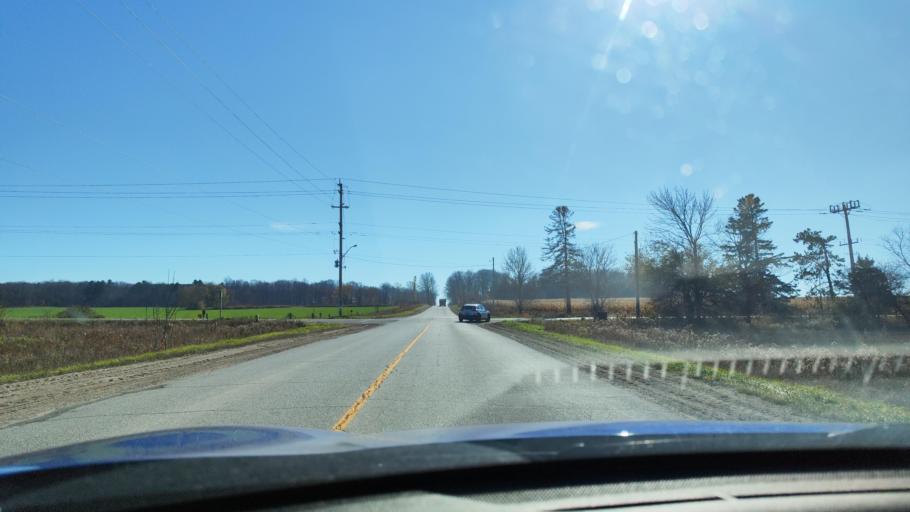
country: CA
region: Ontario
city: Wasaga Beach
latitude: 44.4600
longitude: -80.0033
